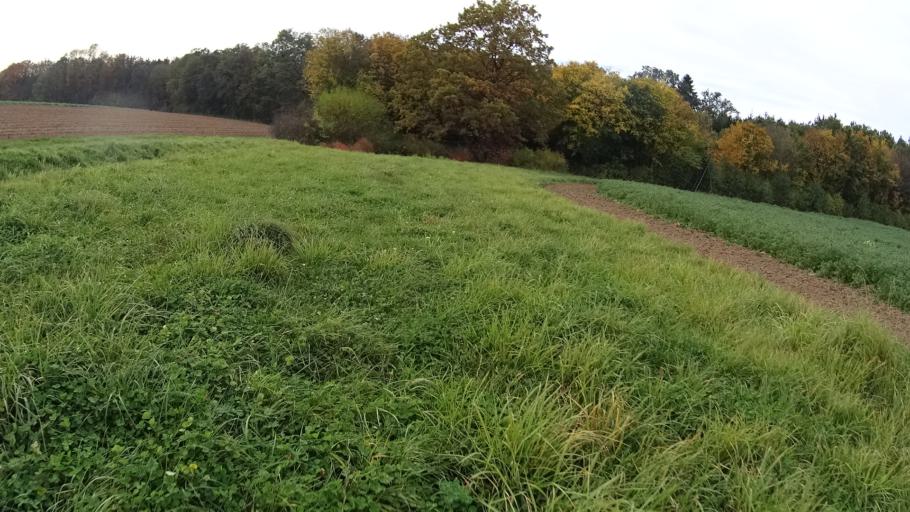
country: DE
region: Bavaria
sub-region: Upper Bavaria
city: Hitzhofen
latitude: 48.8588
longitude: 11.3032
